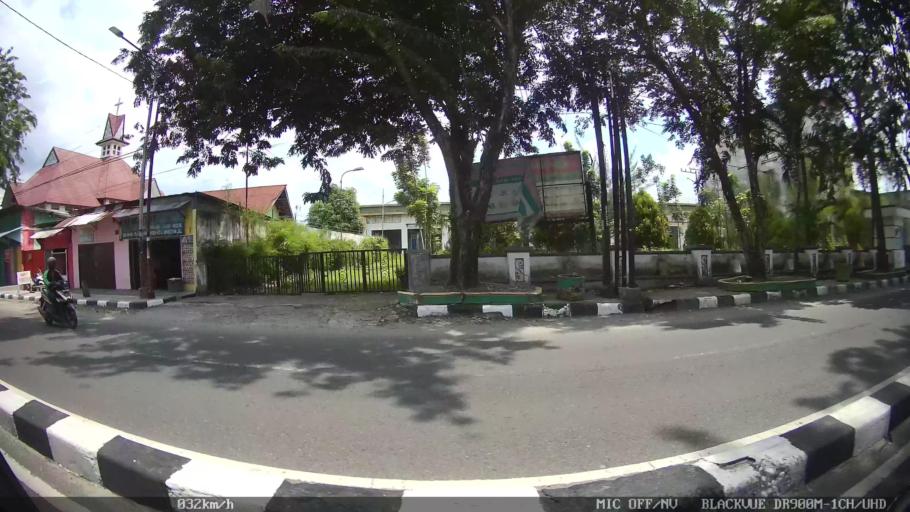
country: ID
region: North Sumatra
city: Medan
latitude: 3.5712
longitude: 98.6640
